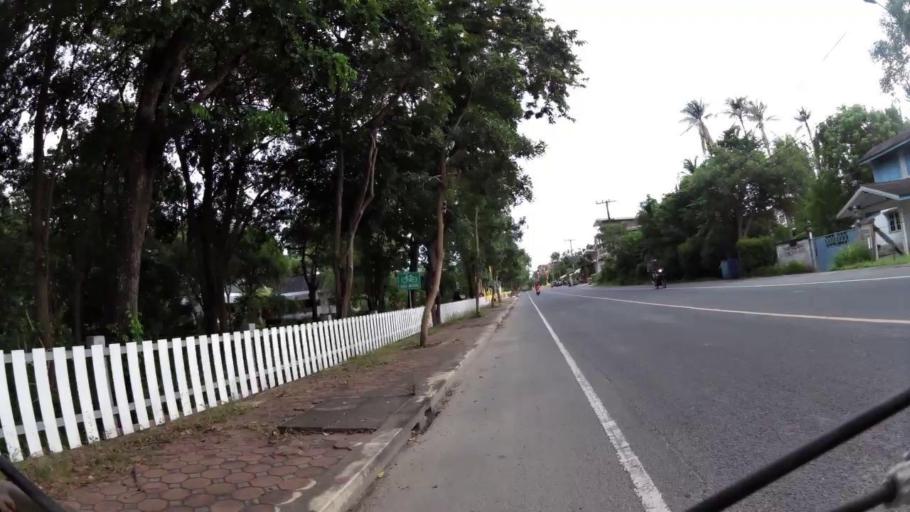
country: TH
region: Prachuap Khiri Khan
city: Prachuap Khiri Khan
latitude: 11.7524
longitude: 99.7903
